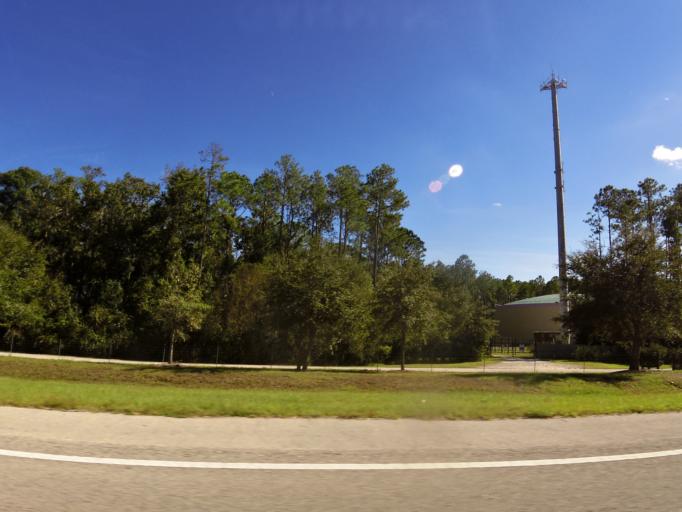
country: US
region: Florida
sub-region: Saint Johns County
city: Palm Valley
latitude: 30.1163
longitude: -81.4108
